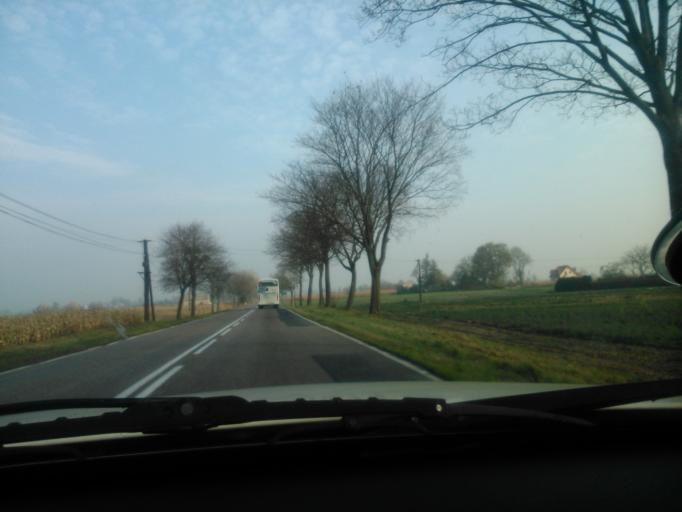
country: PL
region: Kujawsko-Pomorskie
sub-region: Powiat wabrzeski
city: Debowa Laka
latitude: 53.2150
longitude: 19.1855
